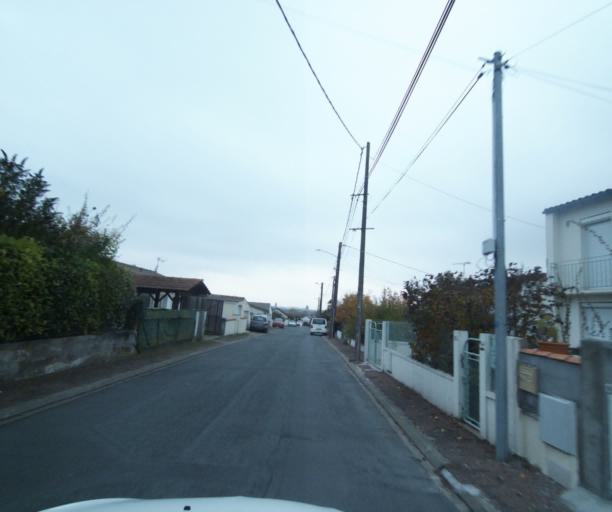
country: FR
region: Poitou-Charentes
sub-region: Departement de la Charente-Maritime
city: Saintes
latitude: 45.7422
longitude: -0.6088
